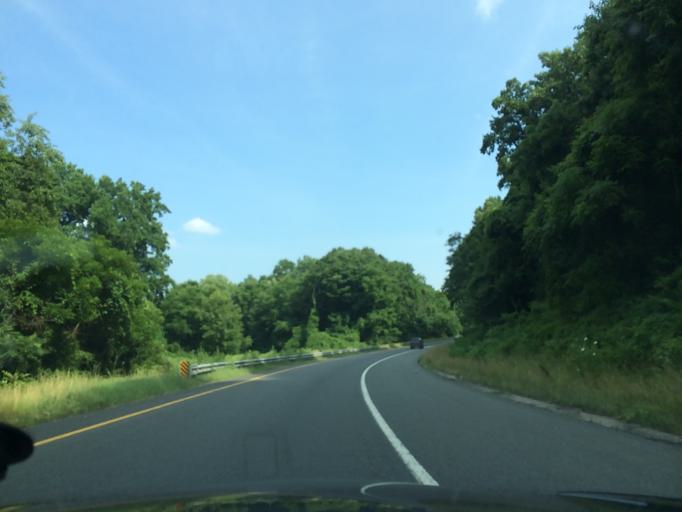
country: US
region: Maryland
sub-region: Howard County
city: Ellicott City
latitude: 39.2958
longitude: -76.8288
